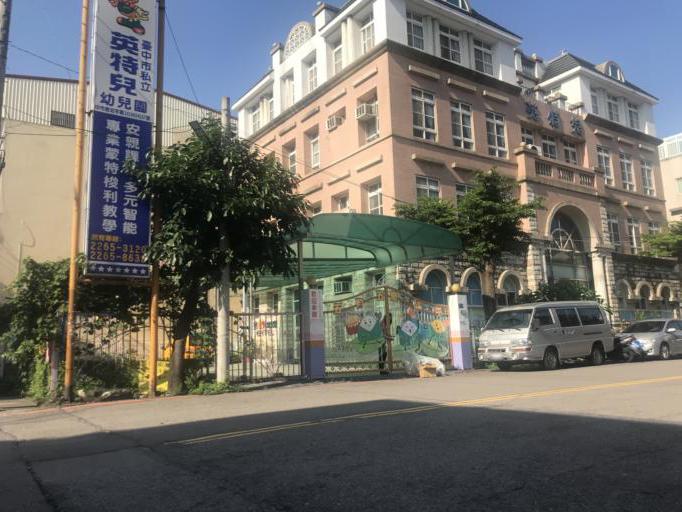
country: TW
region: Taiwan
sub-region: Taichung City
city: Taichung
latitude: 24.1100
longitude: 120.6577
